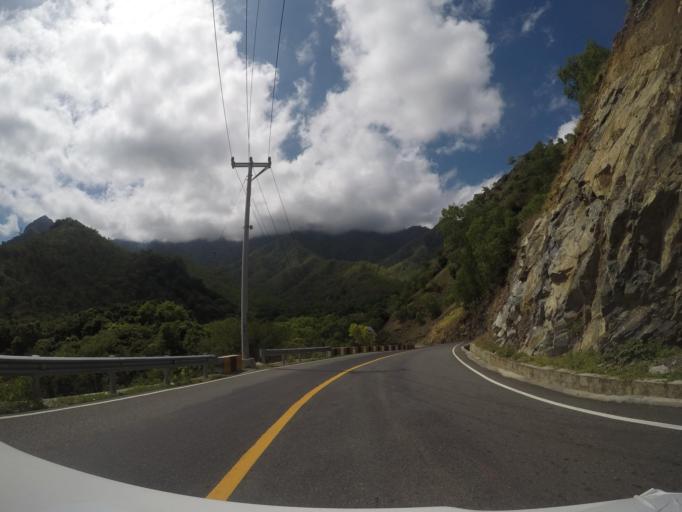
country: TL
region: Manatuto
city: Manatuto
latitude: -8.4778
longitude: 125.9073
